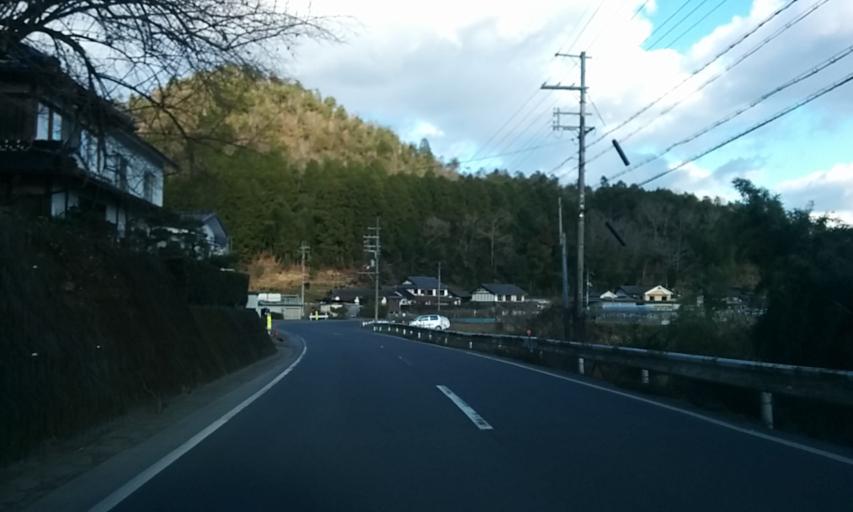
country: JP
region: Kyoto
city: Fukuchiyama
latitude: 35.3120
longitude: 135.1744
